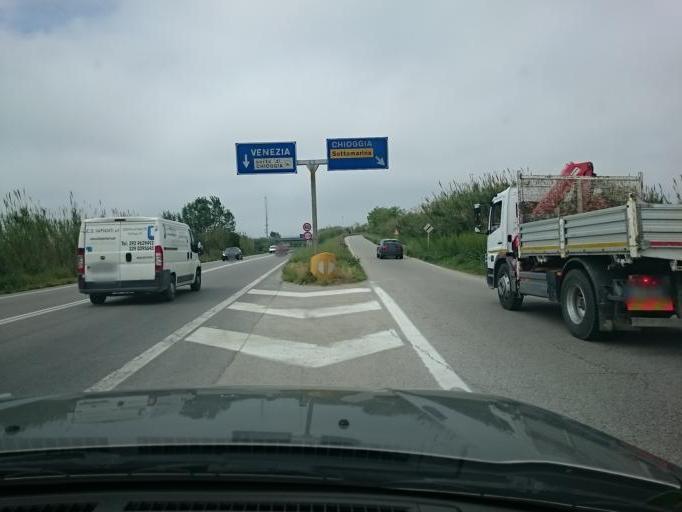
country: IT
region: Veneto
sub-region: Provincia di Venezia
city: Chioggia
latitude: 45.1950
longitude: 12.2743
